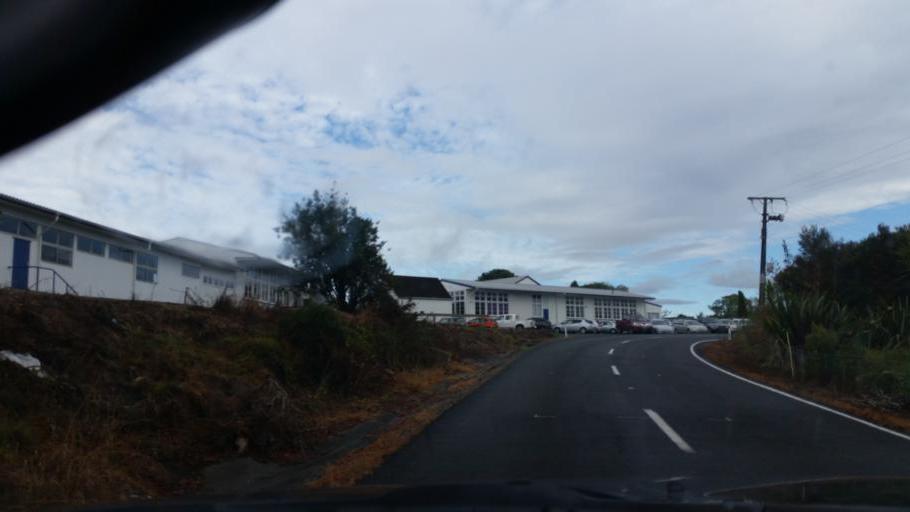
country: NZ
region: Auckland
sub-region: Auckland
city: Wellsford
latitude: -36.1176
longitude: 174.3660
